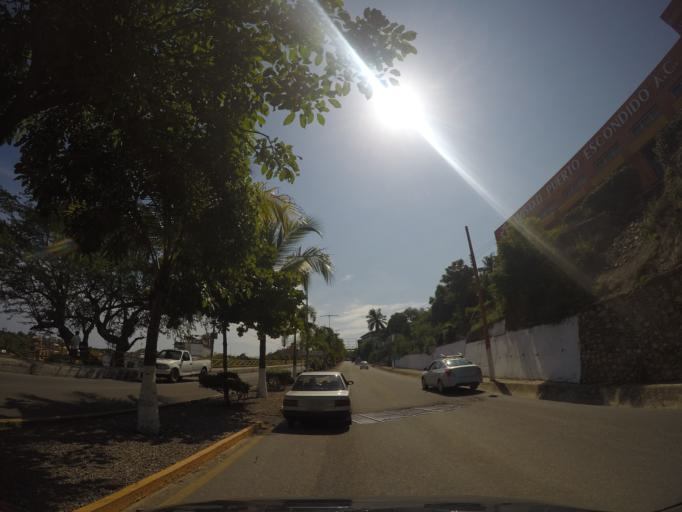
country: MX
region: Oaxaca
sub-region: San Pedro Mixtepec -Dto. 22 -
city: Puerto Escondido
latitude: 15.8622
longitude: -97.0652
